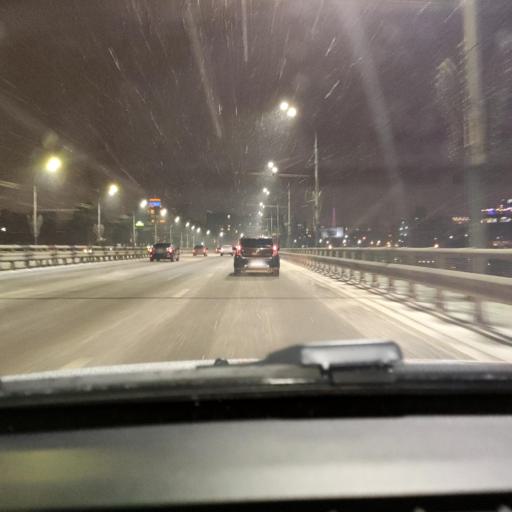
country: RU
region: Voronezj
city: Voronezh
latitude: 51.6690
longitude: 39.2245
